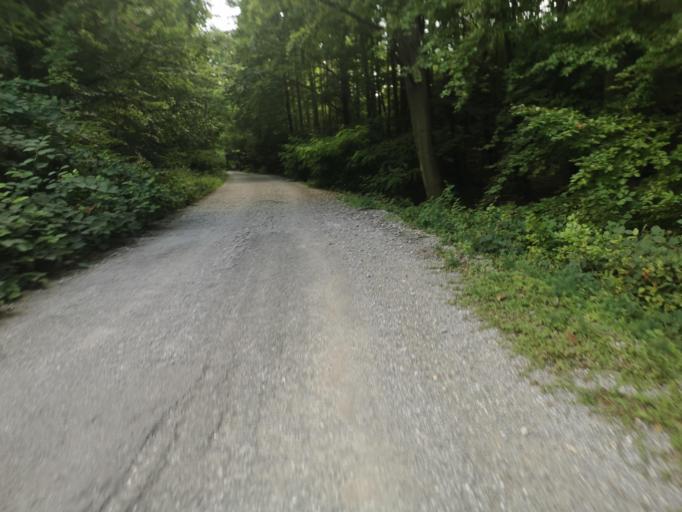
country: SK
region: Trenciansky
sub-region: Okres Myjava
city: Myjava
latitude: 48.7856
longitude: 17.6088
